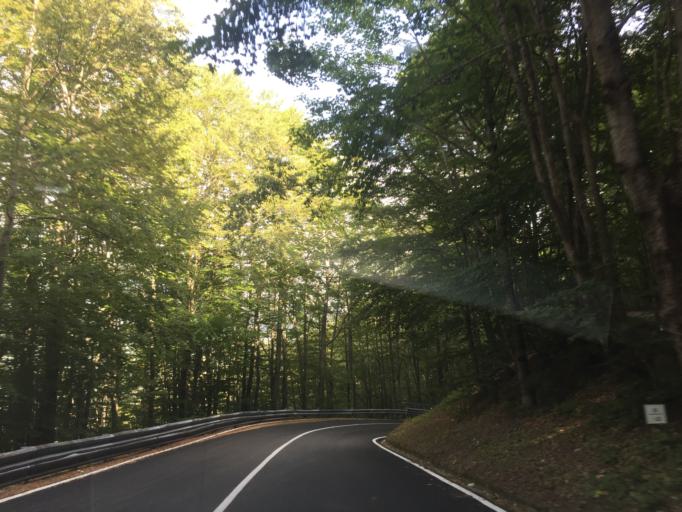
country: IT
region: Tuscany
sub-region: Provincia di Pistoia
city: Cutigliano
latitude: 44.1243
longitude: 10.7126
